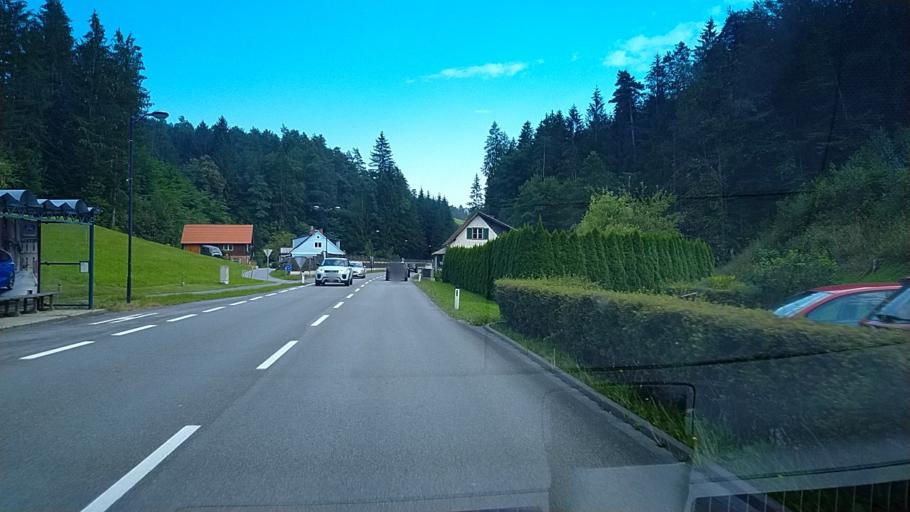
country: AT
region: Styria
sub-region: Politischer Bezirk Deutschlandsberg
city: Sankt Peter im Sulmtal
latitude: 46.7341
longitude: 15.2434
